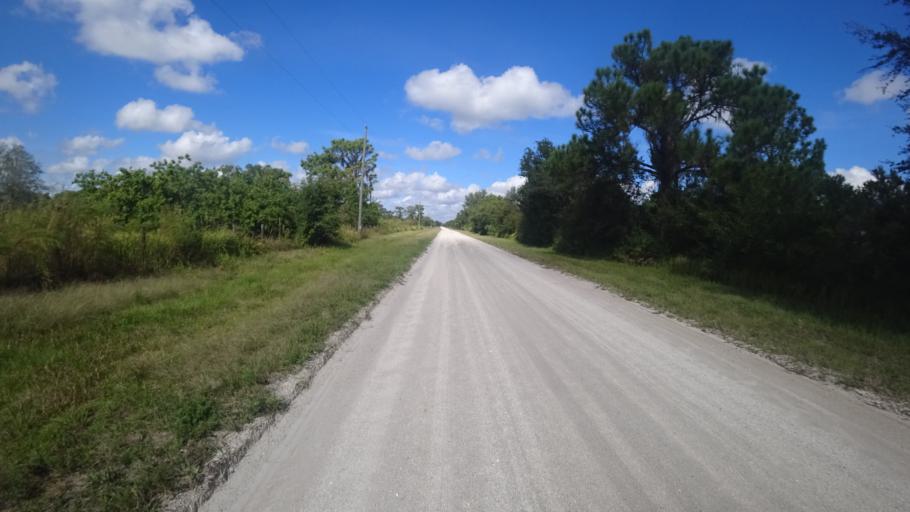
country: US
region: Florida
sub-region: DeSoto County
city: Arcadia
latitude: 27.3565
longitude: -82.1283
